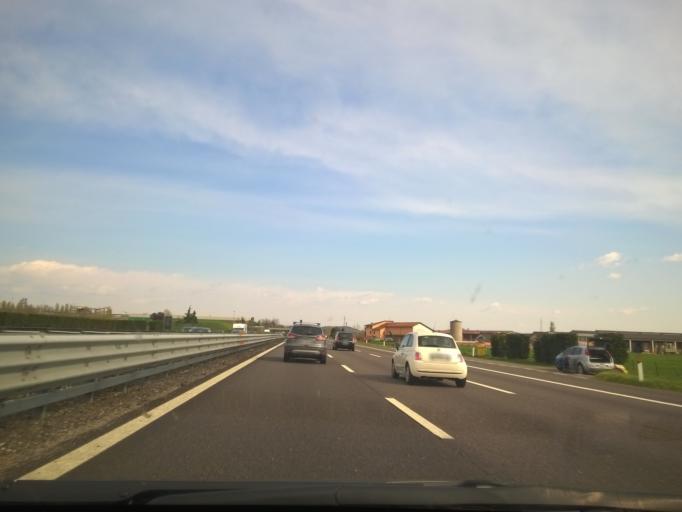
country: IT
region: Lombardy
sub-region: Provincia di Brescia
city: Lonato
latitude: 45.4601
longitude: 10.4459
